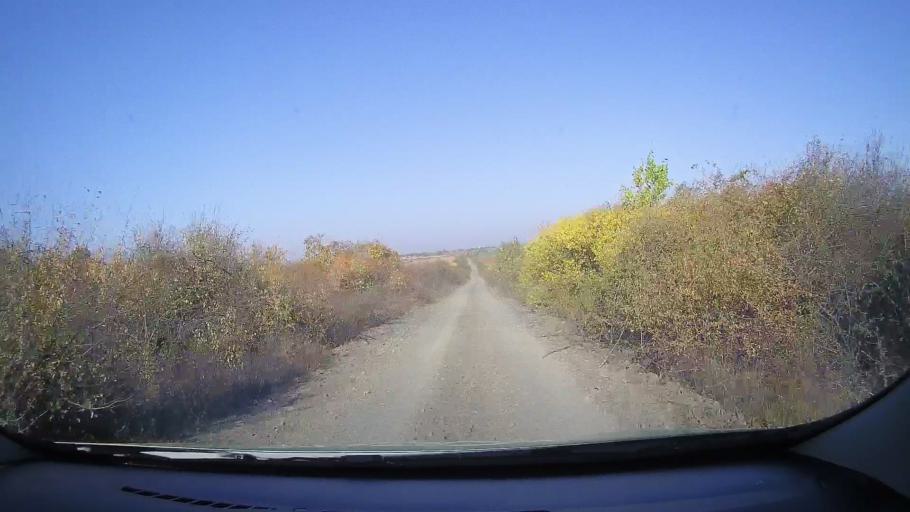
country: RO
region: Satu Mare
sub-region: Comuna Sauca
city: Sauca
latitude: 47.4793
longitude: 22.4717
